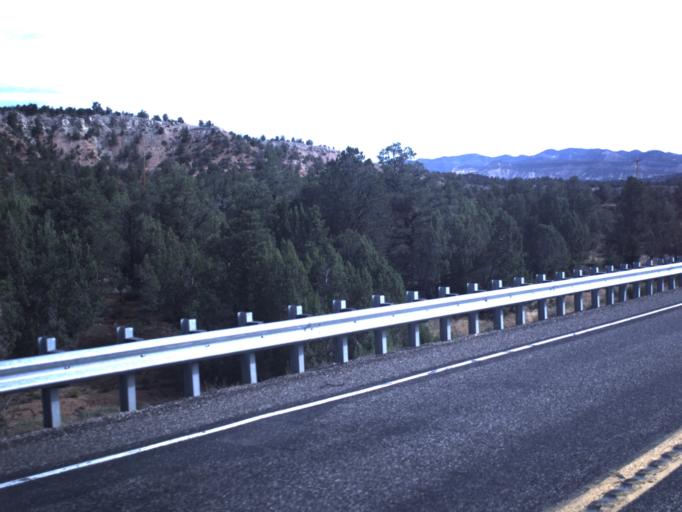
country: US
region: Utah
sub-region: Kane County
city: Kanab
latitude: 37.2214
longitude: -112.6930
